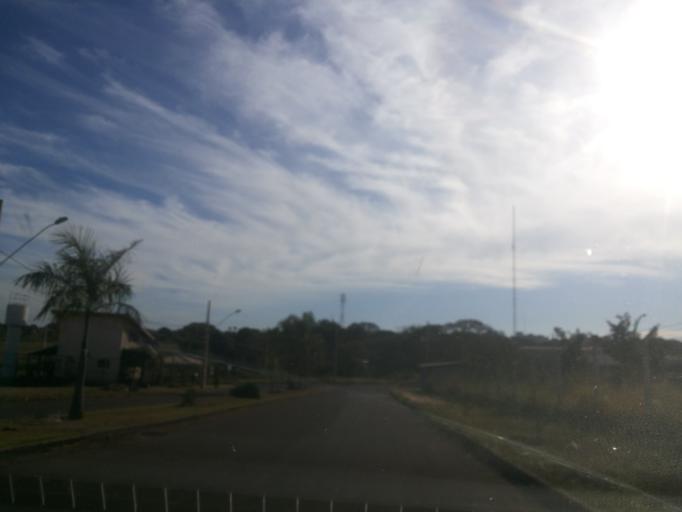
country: BR
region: Minas Gerais
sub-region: Ituiutaba
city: Ituiutaba
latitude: -19.0018
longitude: -49.4596
